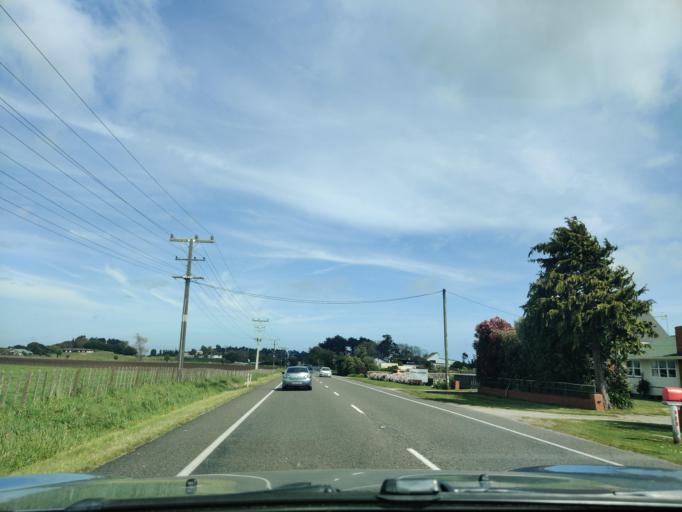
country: NZ
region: Manawatu-Wanganui
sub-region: Wanganui District
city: Wanganui
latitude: -39.8917
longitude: 175.0074
